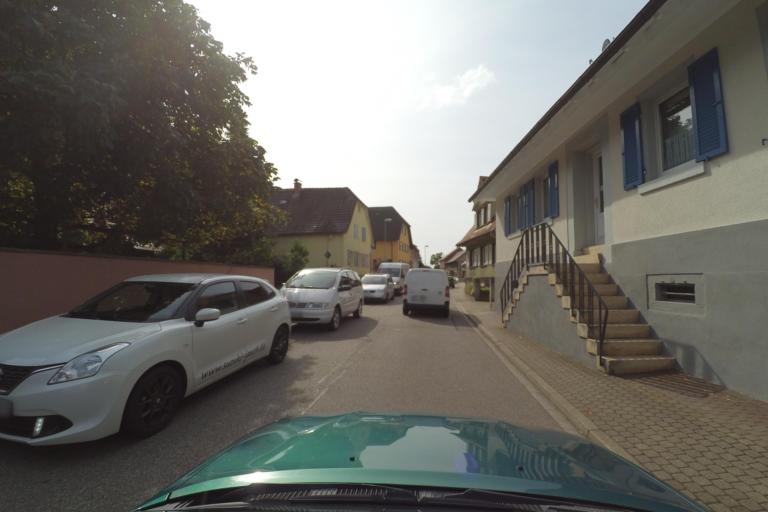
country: DE
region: Baden-Wuerttemberg
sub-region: Freiburg Region
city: Mahlberg
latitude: 48.2880
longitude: 7.8099
